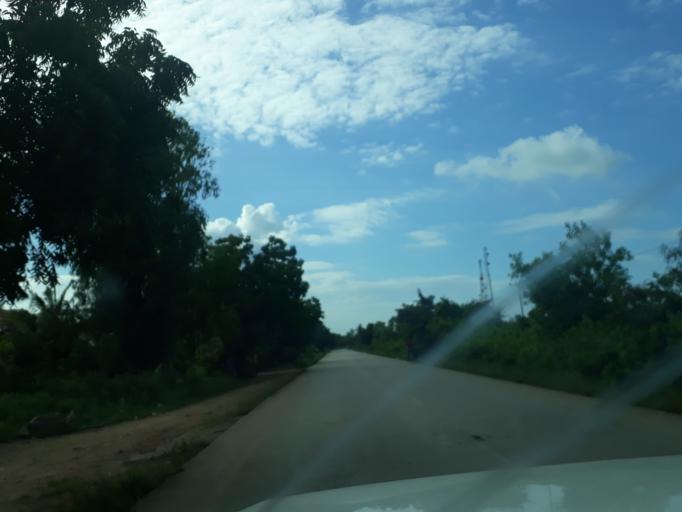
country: TZ
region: Zanzibar North
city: Nungwi
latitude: -5.7680
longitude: 39.3015
